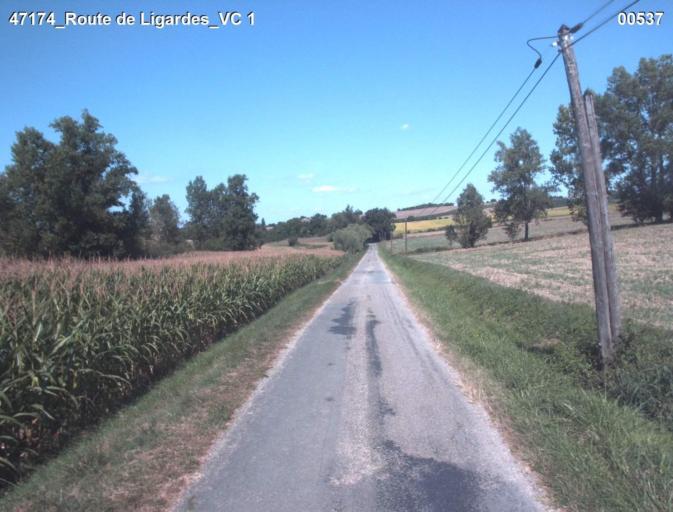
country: FR
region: Midi-Pyrenees
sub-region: Departement du Gers
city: Condom
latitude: 44.0296
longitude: 0.4121
